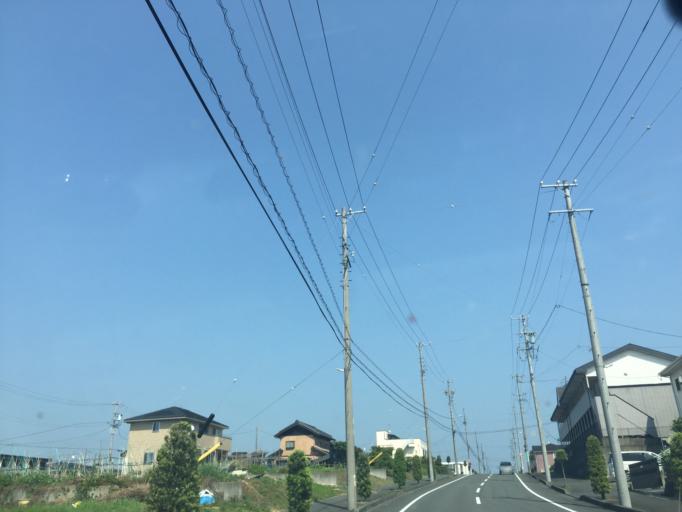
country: JP
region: Shizuoka
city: Kakegawa
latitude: 34.7638
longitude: 138.0257
